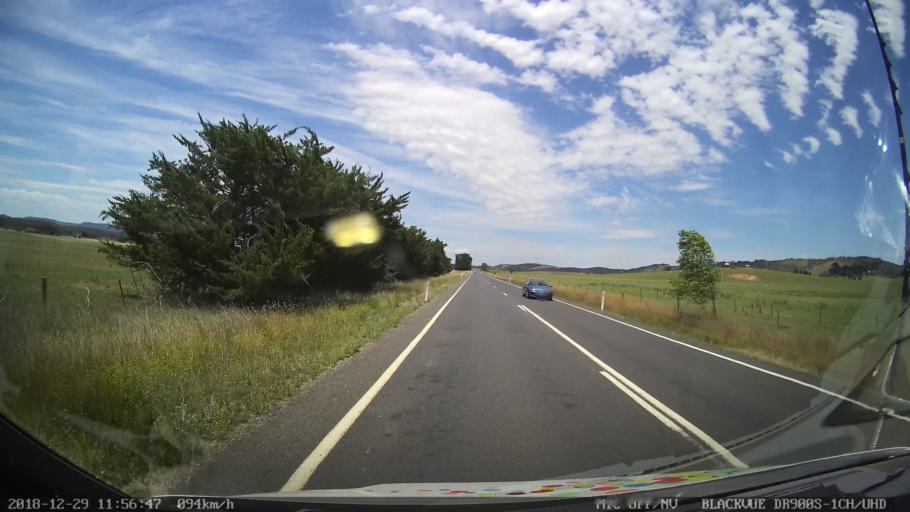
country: AU
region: New South Wales
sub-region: Palerang
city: Bungendore
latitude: -35.2804
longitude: 149.4225
